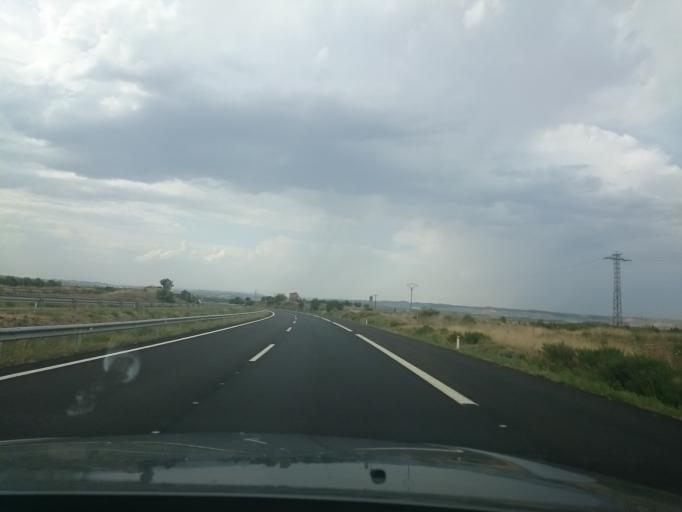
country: ES
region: La Rioja
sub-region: Provincia de La Rioja
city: Aldeanueva de Ebro
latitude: 42.2428
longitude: -1.9011
